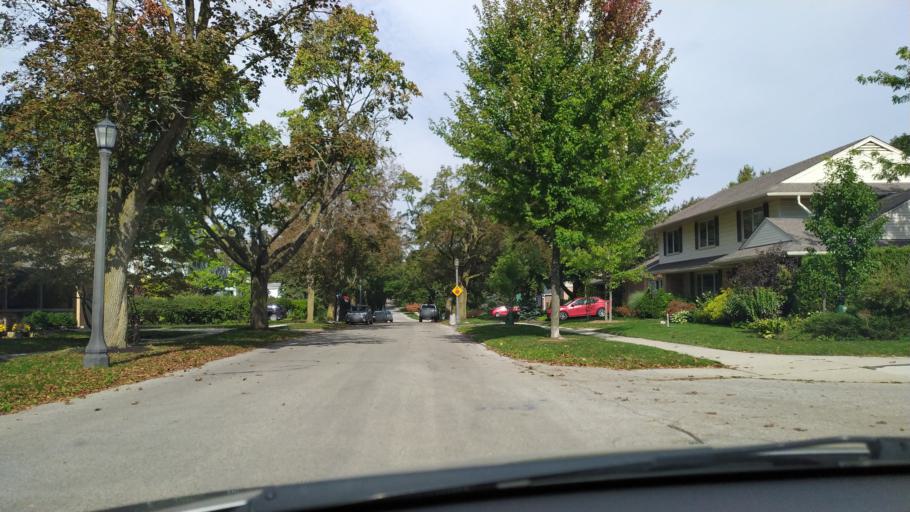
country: CA
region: Ontario
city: Waterloo
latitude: 43.4521
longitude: -80.5215
